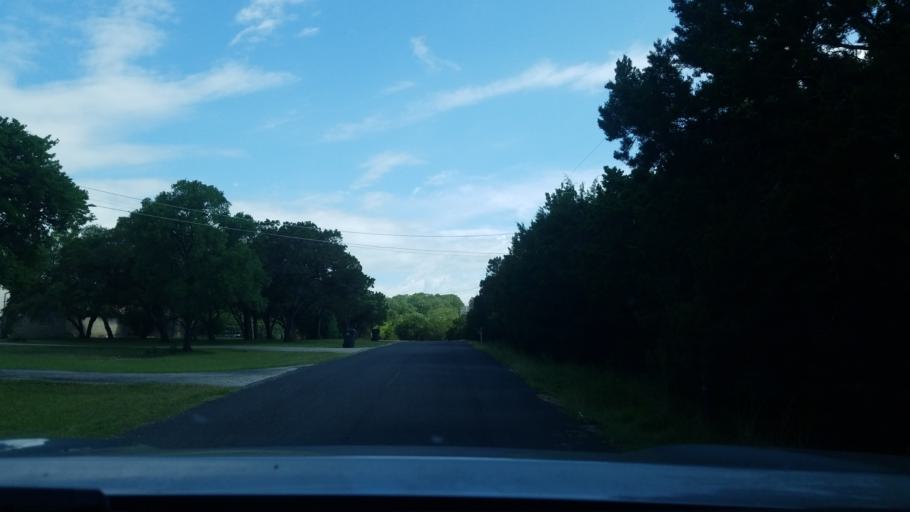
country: US
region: Texas
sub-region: Comal County
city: Bulverde
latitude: 29.7527
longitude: -98.4427
